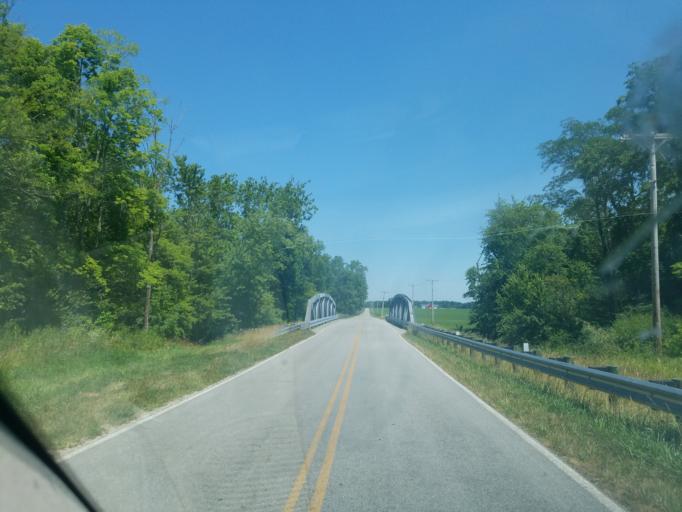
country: US
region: Ohio
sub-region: Mercer County
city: Rockford
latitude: 40.7336
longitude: -84.7370
